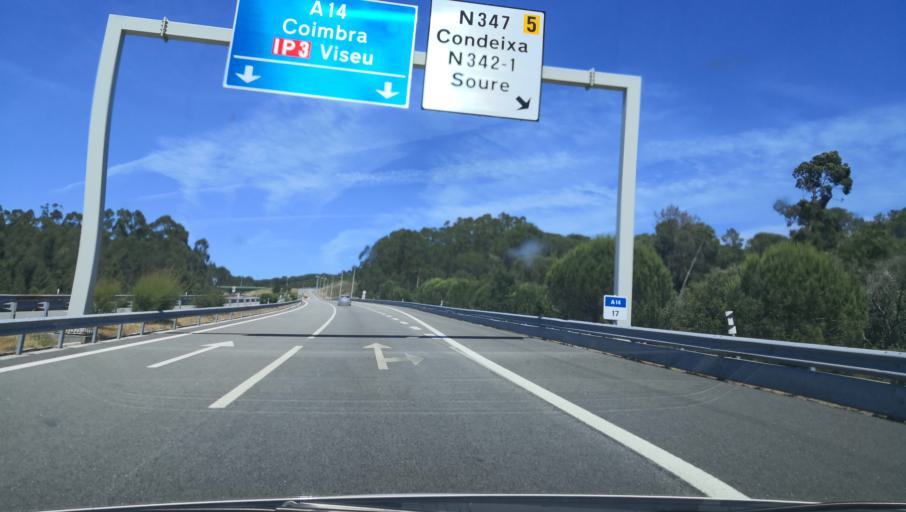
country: PT
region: Coimbra
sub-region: Montemor-O-Velho
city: Montemor-o-Velho
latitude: 40.1983
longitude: -8.6794
